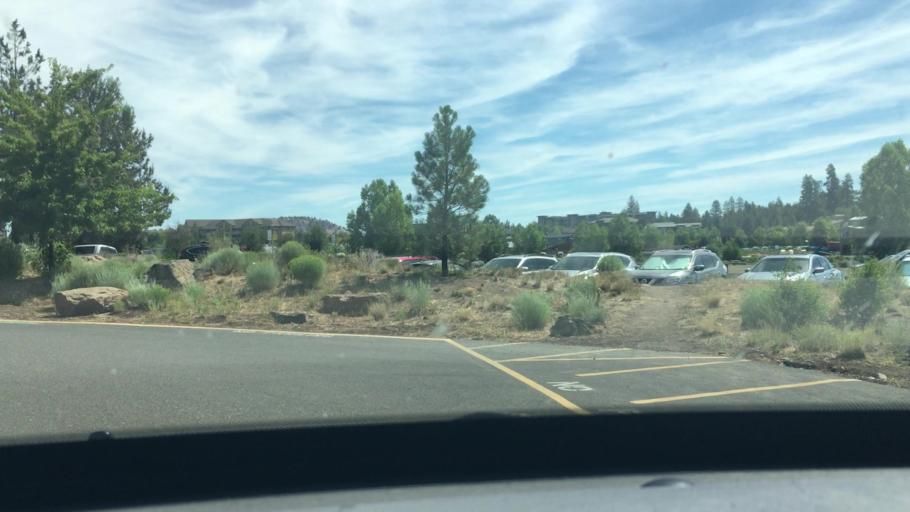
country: US
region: Oregon
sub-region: Deschutes County
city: Bend
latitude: 44.0428
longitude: -121.3195
